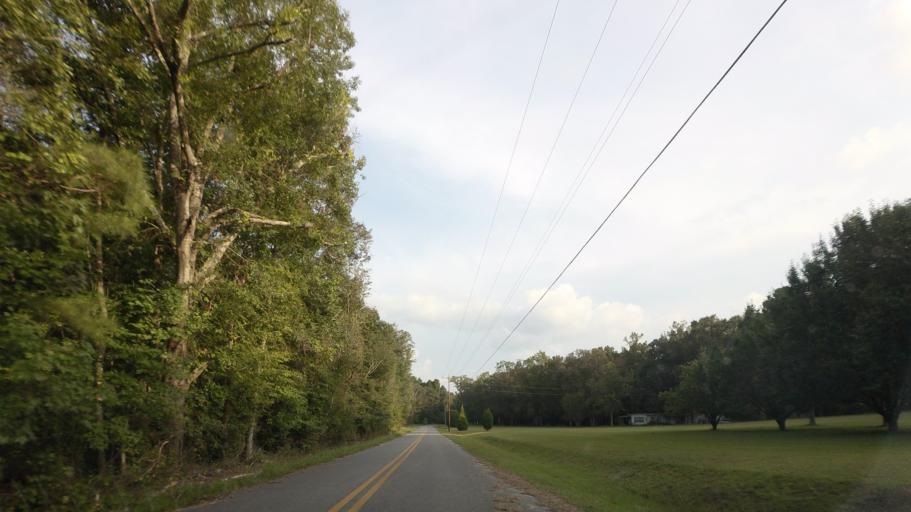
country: US
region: Georgia
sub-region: Wilkinson County
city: Gordon
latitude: 32.8320
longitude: -83.3923
